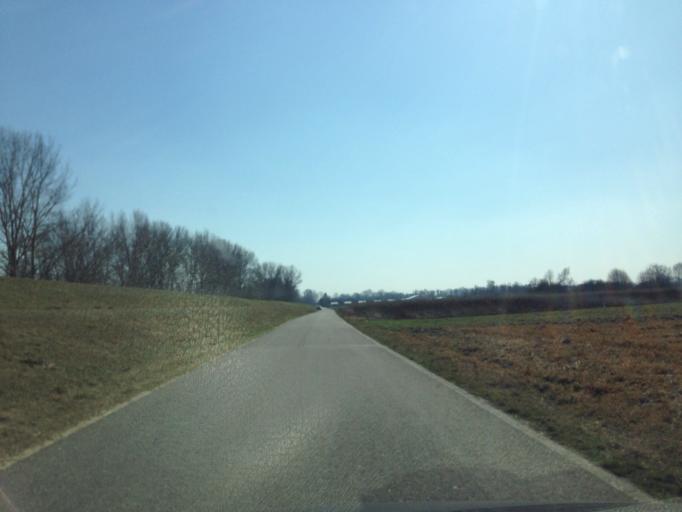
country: PL
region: Masovian Voivodeship
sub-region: Warszawa
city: Wawer
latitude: 52.1351
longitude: 21.1650
